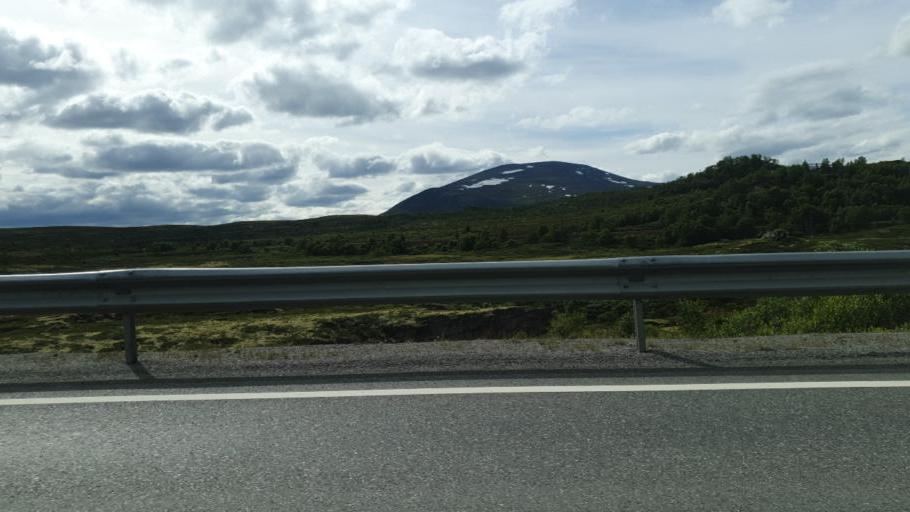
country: NO
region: Sor-Trondelag
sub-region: Oppdal
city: Oppdal
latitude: 62.2831
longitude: 9.5995
